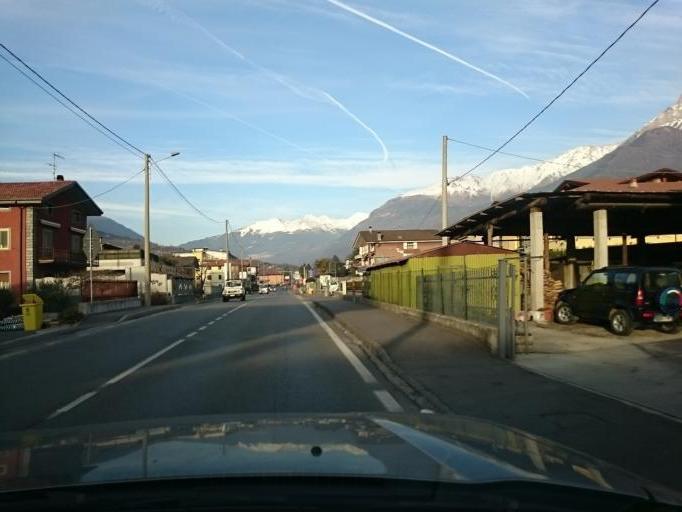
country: IT
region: Lombardy
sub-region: Provincia di Brescia
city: Losine
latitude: 45.9778
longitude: 10.3222
